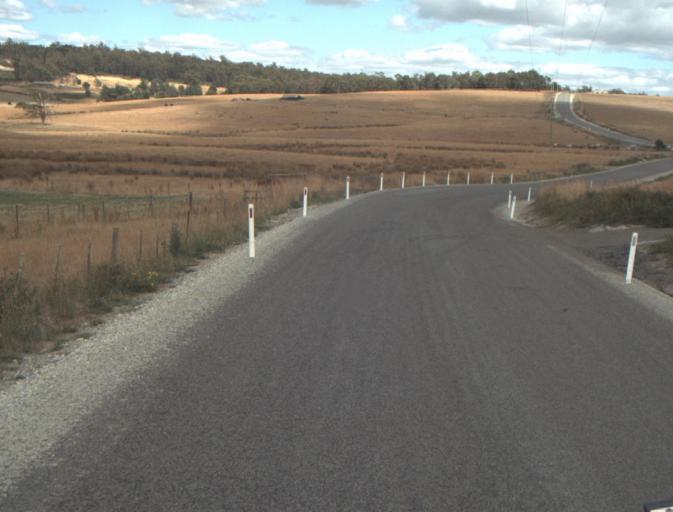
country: AU
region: Tasmania
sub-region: Launceston
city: Mayfield
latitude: -41.1929
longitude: 147.1773
